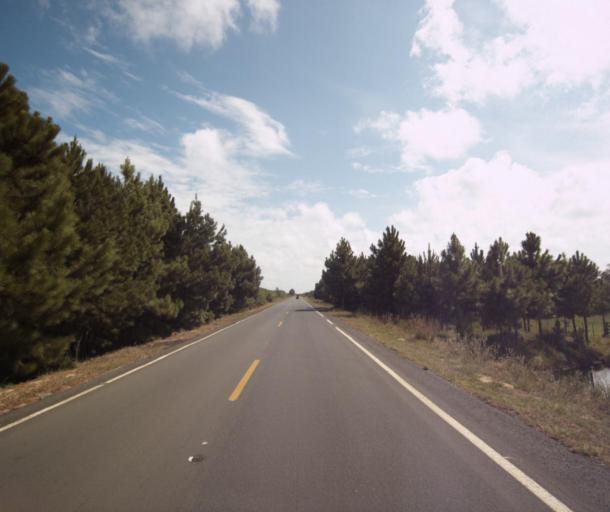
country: BR
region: Rio Grande do Sul
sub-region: Sao Lourenco Do Sul
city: Sao Lourenco do Sul
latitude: -31.4459
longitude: -51.2057
